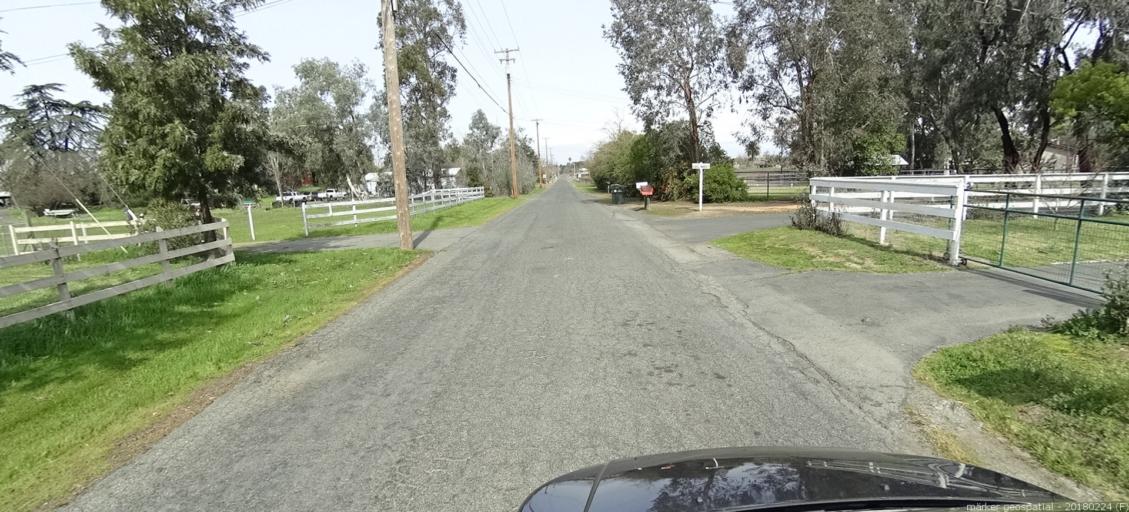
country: US
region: California
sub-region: Sacramento County
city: Elverta
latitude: 38.6957
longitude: -121.4708
